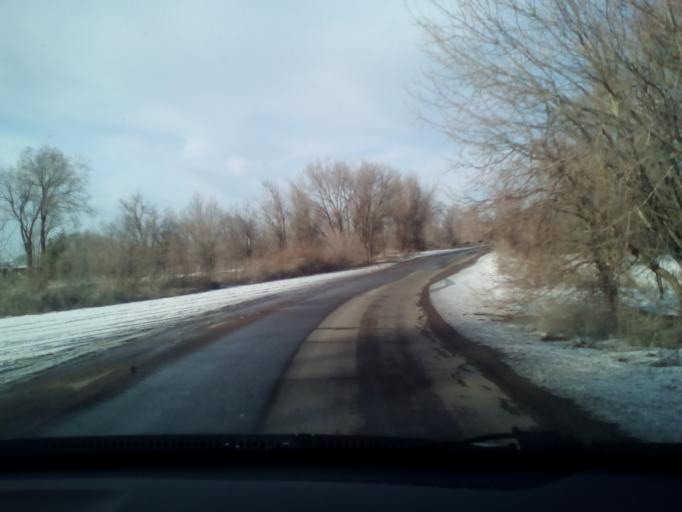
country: KZ
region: Almaty Oblysy
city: Burunday
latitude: 43.2206
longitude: 76.4100
